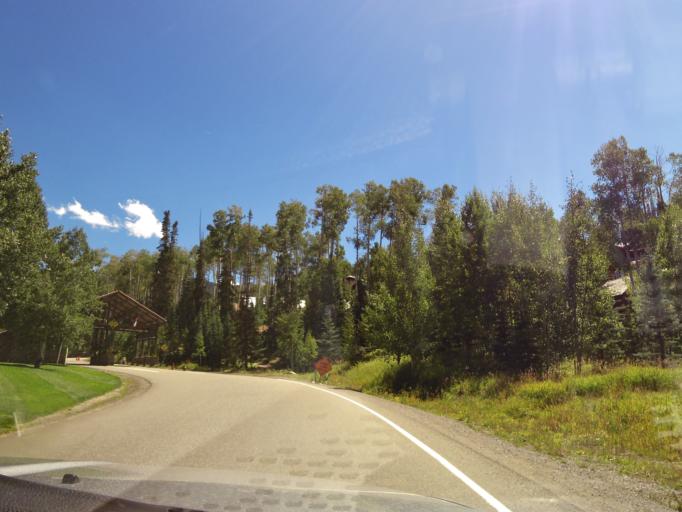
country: US
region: Colorado
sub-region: San Miguel County
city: Mountain Village
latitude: 37.9327
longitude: -107.8565
